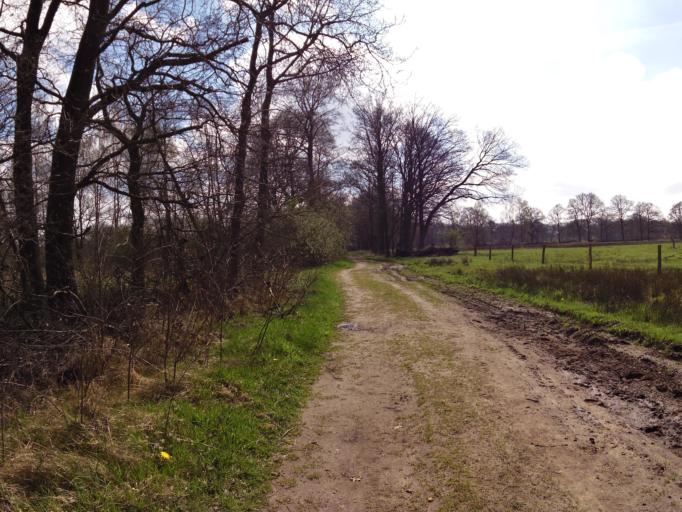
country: NL
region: North Brabant
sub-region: Gemeente Haaren
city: Haaren
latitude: 51.5582
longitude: 5.2642
